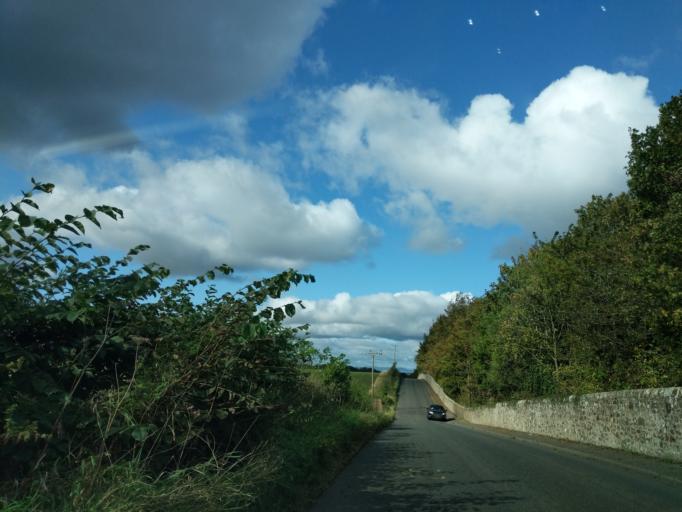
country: GB
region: Scotland
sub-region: Edinburgh
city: Currie
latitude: 55.9059
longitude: -3.3277
